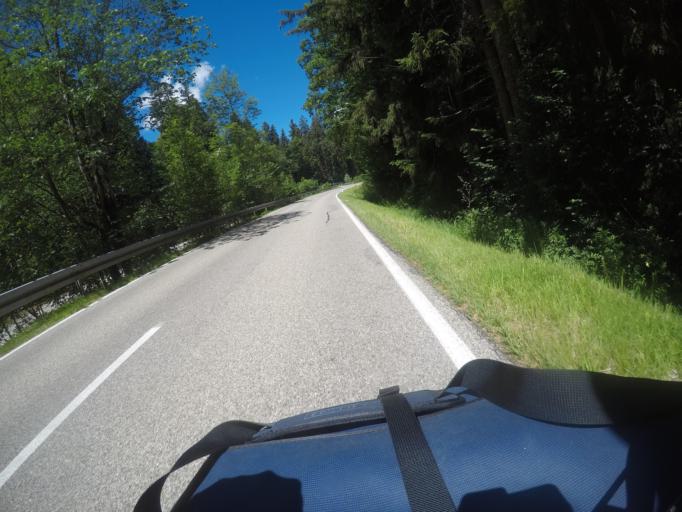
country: DE
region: Bavaria
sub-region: Upper Bavaria
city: Prem
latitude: 47.6542
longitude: 10.7883
